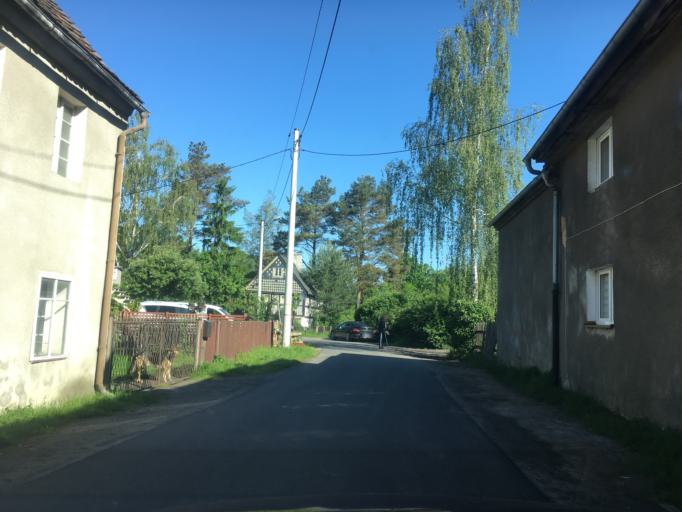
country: PL
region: Lower Silesian Voivodeship
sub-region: Powiat zgorzelecki
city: Sulikow
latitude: 51.0750
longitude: 15.0657
